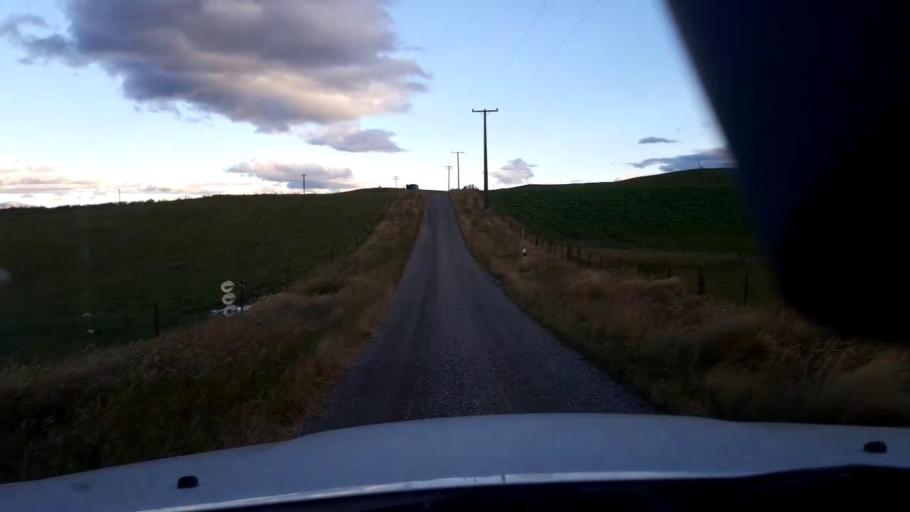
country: NZ
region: Canterbury
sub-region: Timaru District
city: Pleasant Point
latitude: -44.2481
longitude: 170.9086
